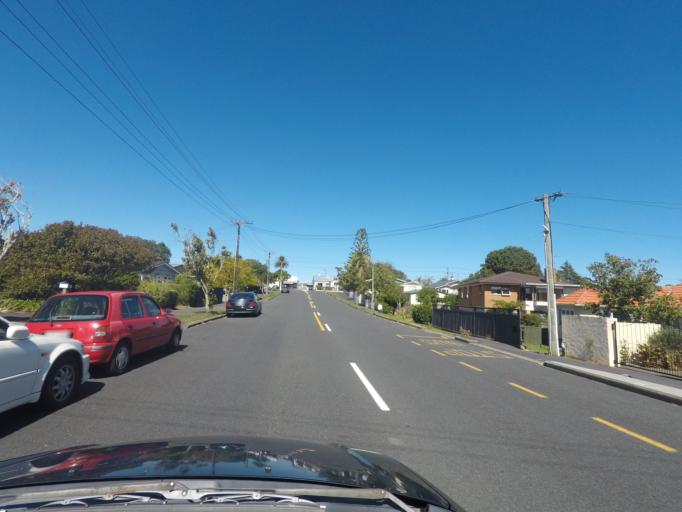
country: NZ
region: Auckland
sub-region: Auckland
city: Rosebank
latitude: -36.9004
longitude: 174.7054
